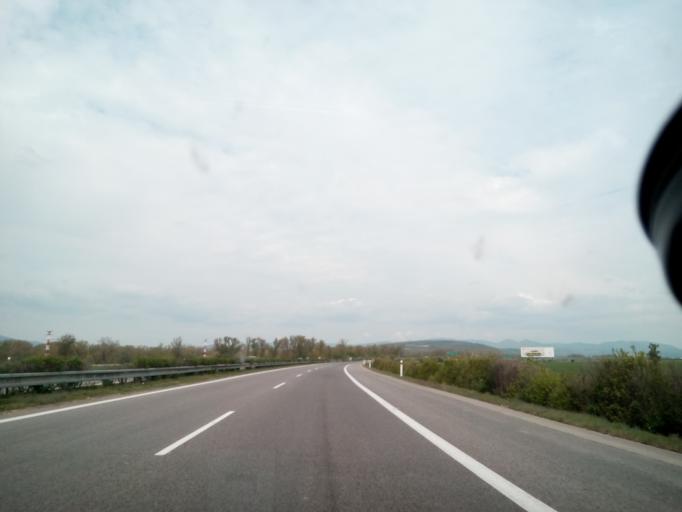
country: SK
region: Trenciansky
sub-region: Okres Nove Mesto nad Vahom
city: Nove Mesto nad Vahom
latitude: 48.7411
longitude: 17.8609
